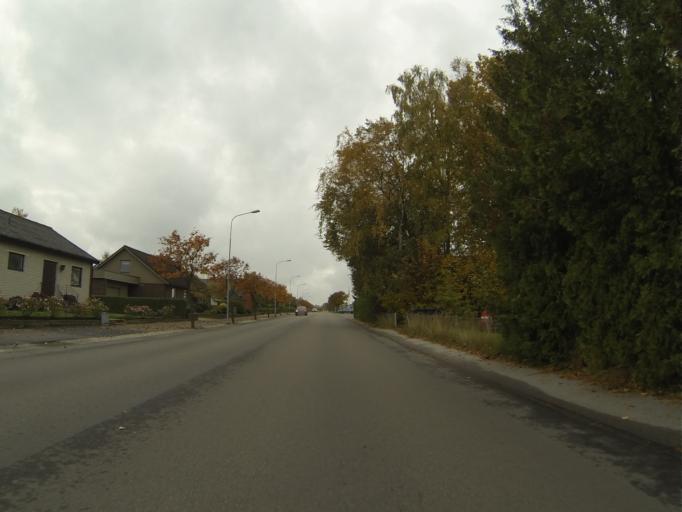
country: SE
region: Skane
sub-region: Sjobo Kommun
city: Sjoebo
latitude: 55.6339
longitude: 13.6915
